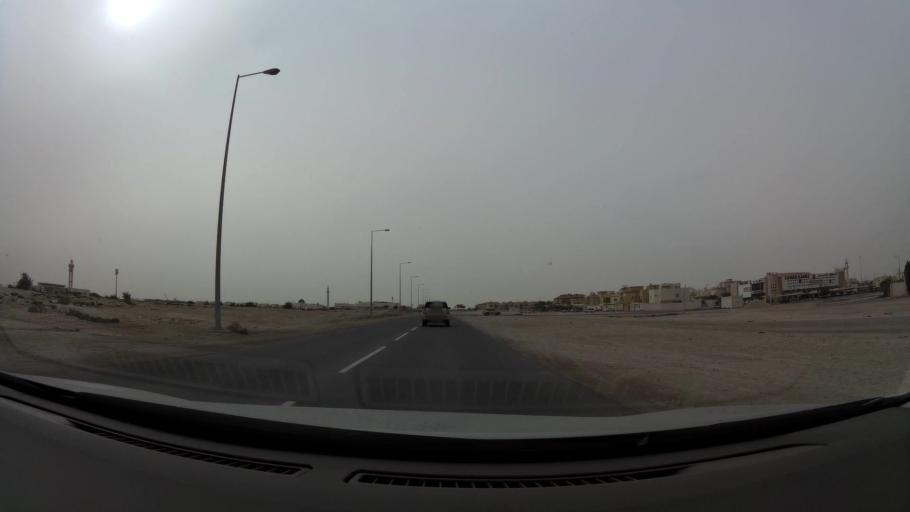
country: QA
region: Baladiyat ad Dawhah
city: Doha
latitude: 25.2405
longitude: 51.5152
